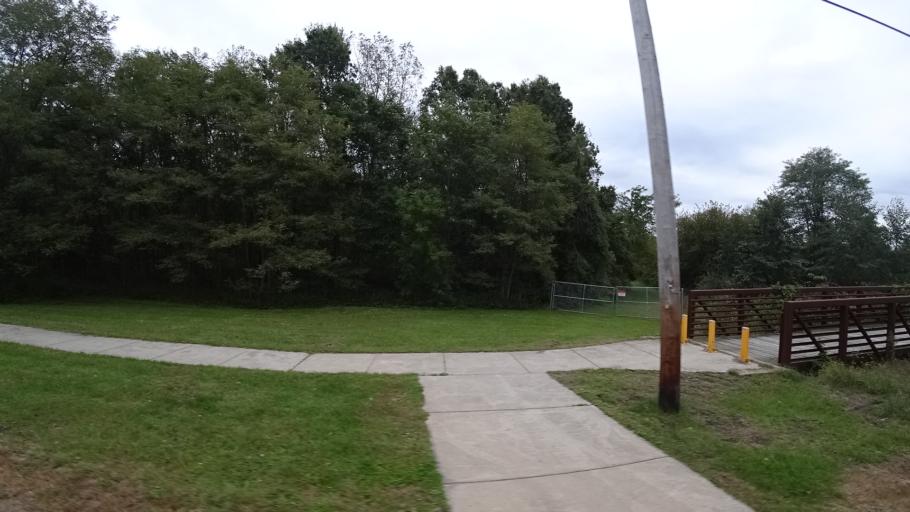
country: US
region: Indiana
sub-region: LaPorte County
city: Michigan City
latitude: 41.6916
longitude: -86.9102
